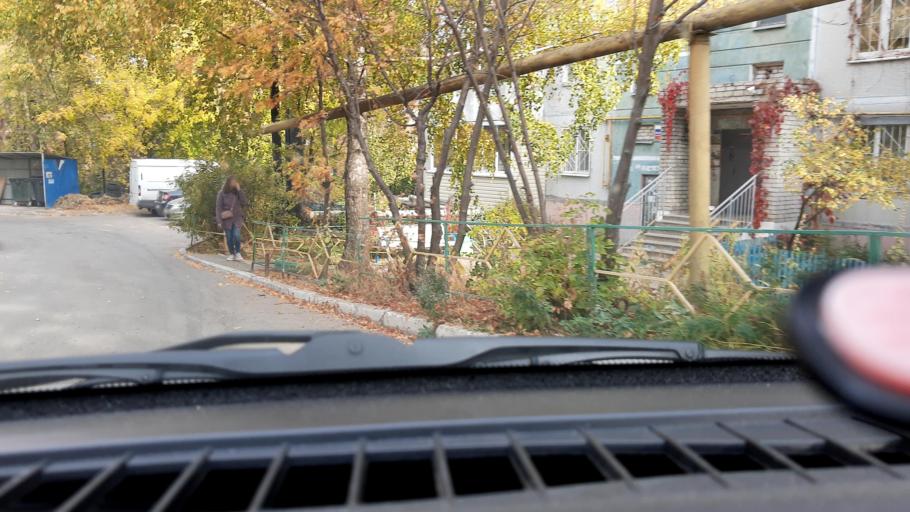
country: RU
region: Nizjnij Novgorod
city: Afonino
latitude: 56.2743
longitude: 44.0877
